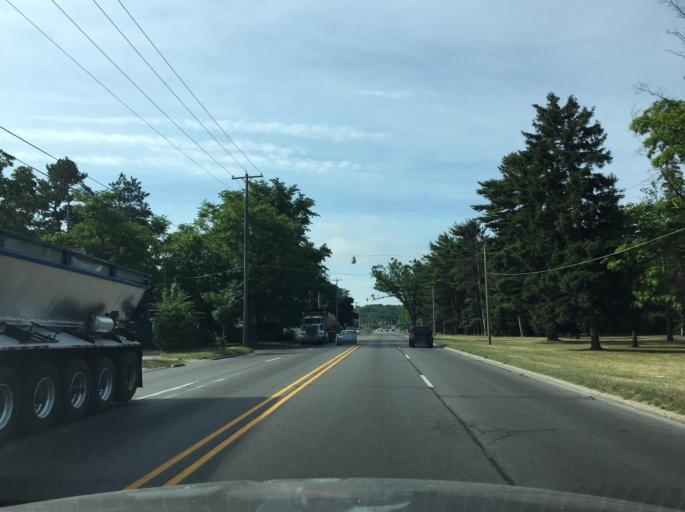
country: US
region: Michigan
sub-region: Grand Traverse County
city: Traverse City
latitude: 44.7557
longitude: -85.6349
